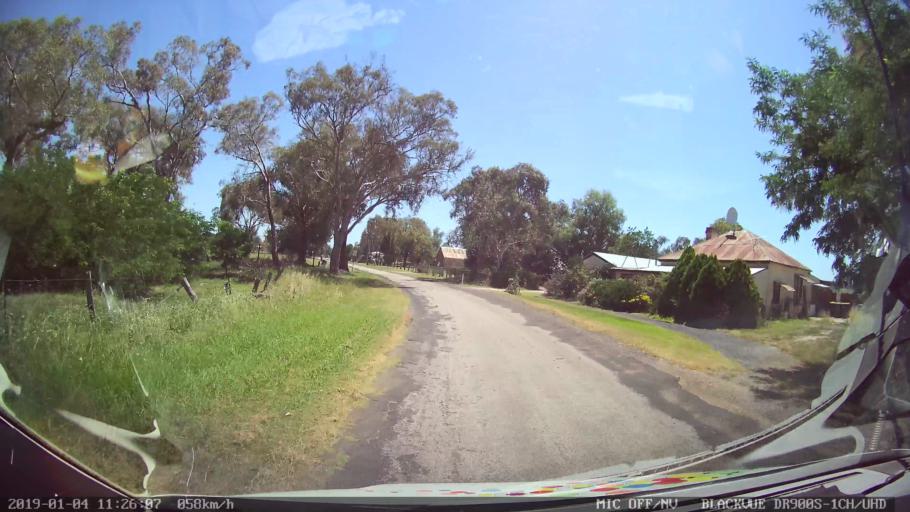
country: AU
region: New South Wales
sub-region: Cabonne
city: Molong
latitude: -33.1175
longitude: 148.7552
